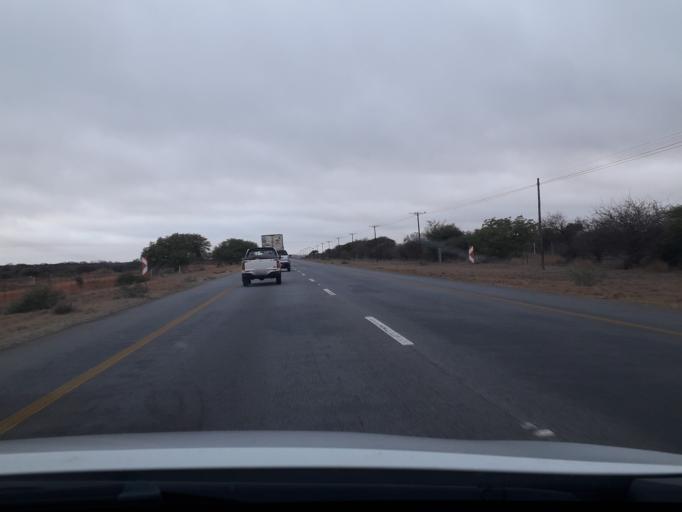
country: ZA
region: Limpopo
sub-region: Capricorn District Municipality
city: Mankoeng
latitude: -23.5800
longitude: 29.6696
